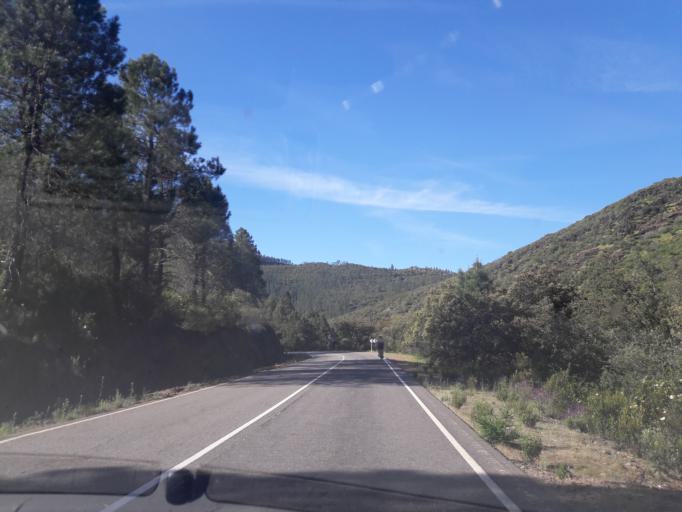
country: ES
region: Castille and Leon
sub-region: Provincia de Salamanca
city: Sotoserrano
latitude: 40.4127
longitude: -6.0530
